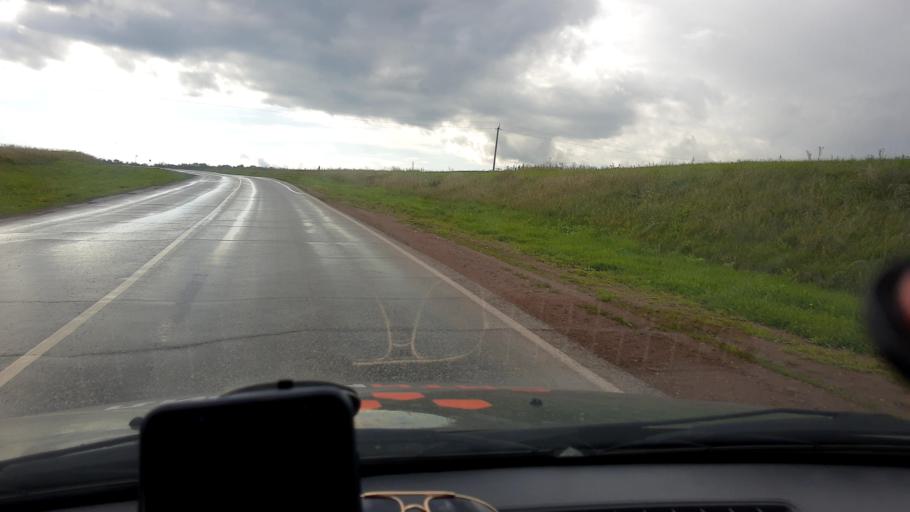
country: RU
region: Bashkortostan
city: Karmaskaly
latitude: 53.9300
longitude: 56.4095
